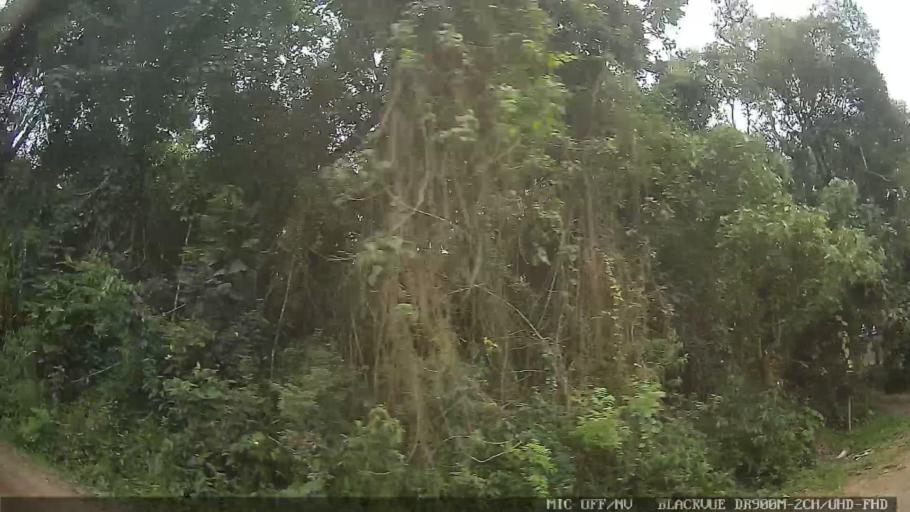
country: BR
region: Sao Paulo
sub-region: Suzano
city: Suzano
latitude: -23.5286
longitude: -46.2553
